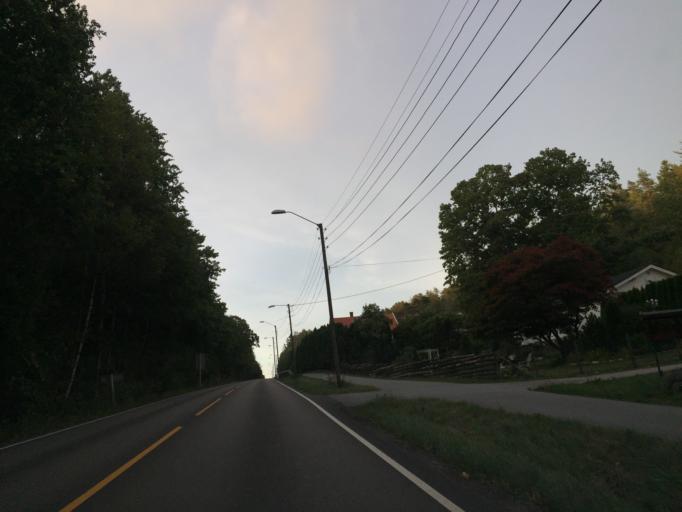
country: NO
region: Ostfold
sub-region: Fredrikstad
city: Fredrikstad
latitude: 59.1838
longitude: 10.9272
